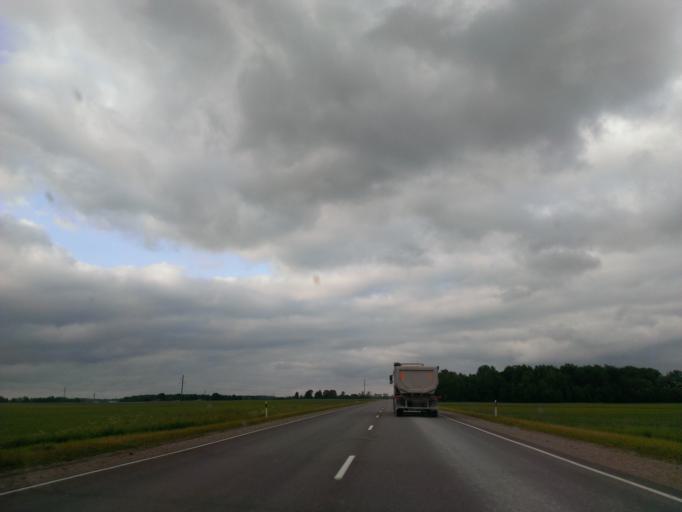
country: LV
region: Saldus Rajons
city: Saldus
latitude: 56.6709
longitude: 22.4285
